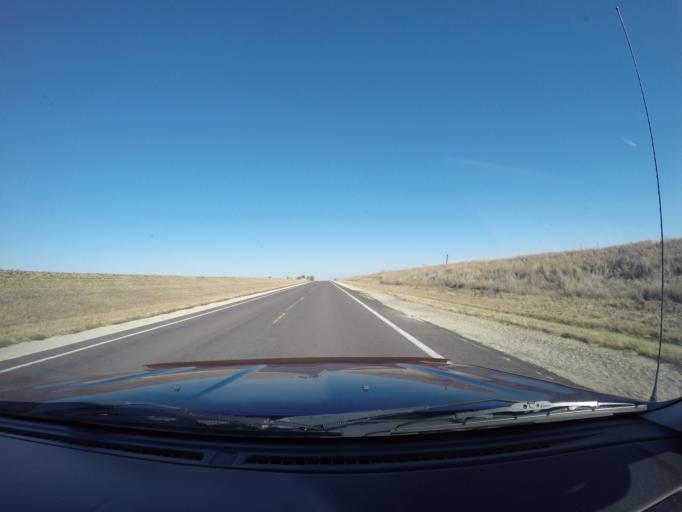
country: US
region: Kansas
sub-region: Marshall County
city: Blue Rapids
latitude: 39.6291
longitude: -96.7503
